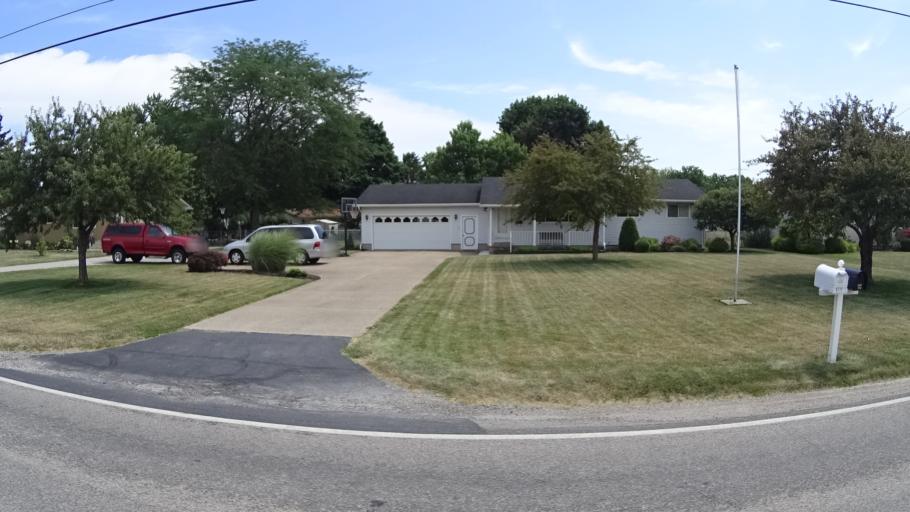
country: US
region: Ohio
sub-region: Erie County
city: Sandusky
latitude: 41.3982
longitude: -82.7834
